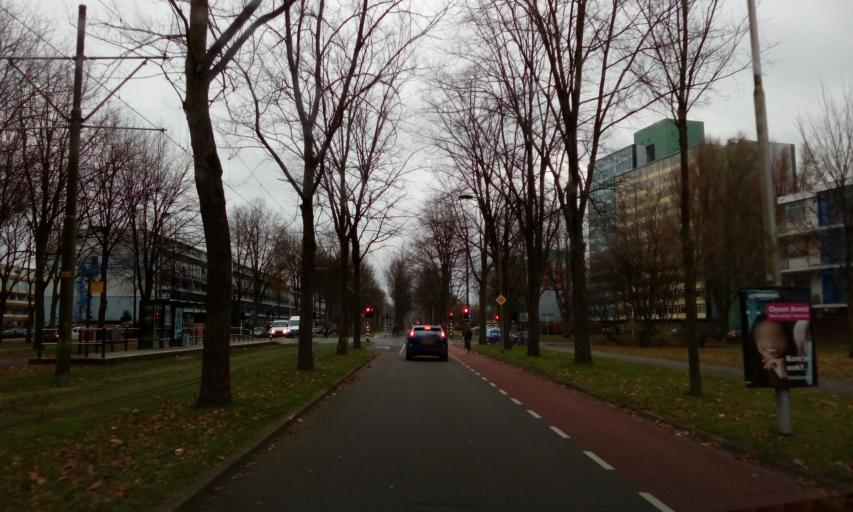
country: NL
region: South Holland
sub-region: Gemeente Delft
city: Delft
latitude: 51.9907
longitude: 4.3444
